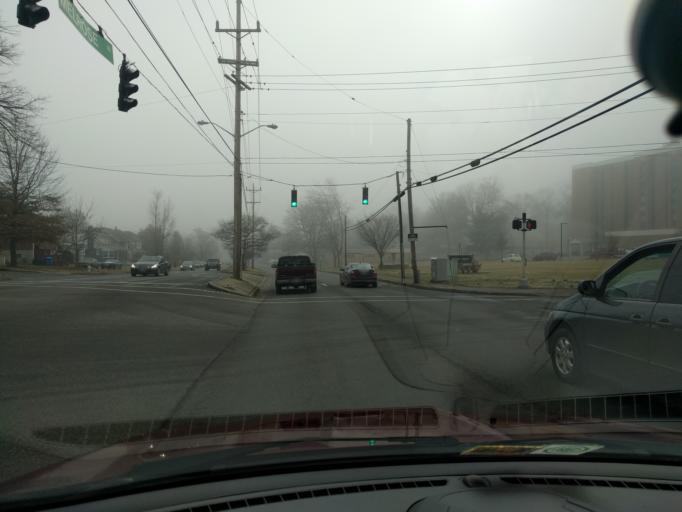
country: US
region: Virginia
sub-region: City of Roanoke
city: Roanoke
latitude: 37.2896
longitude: -79.9867
